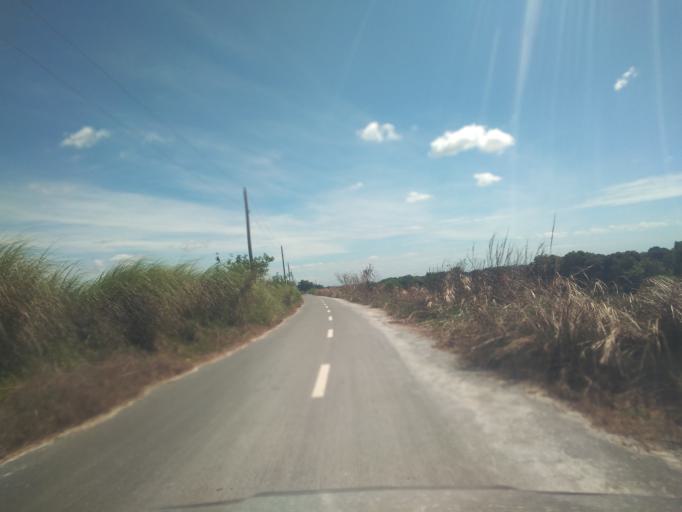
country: PH
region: Central Luzon
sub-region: Province of Pampanga
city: Balas
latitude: 15.0536
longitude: 120.5762
